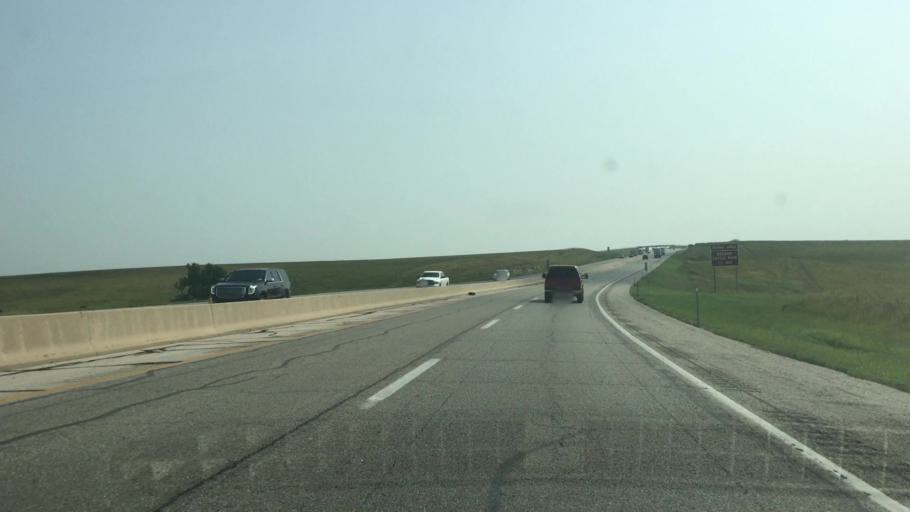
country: US
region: Kansas
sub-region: Chase County
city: Cottonwood Falls
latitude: 38.2258
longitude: -96.4251
